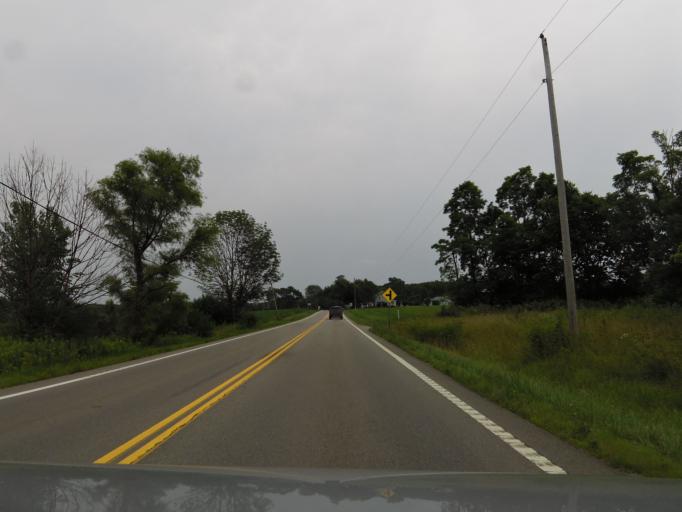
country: US
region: Ohio
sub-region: Warren County
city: Waynesville
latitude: 39.4974
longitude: -83.9867
